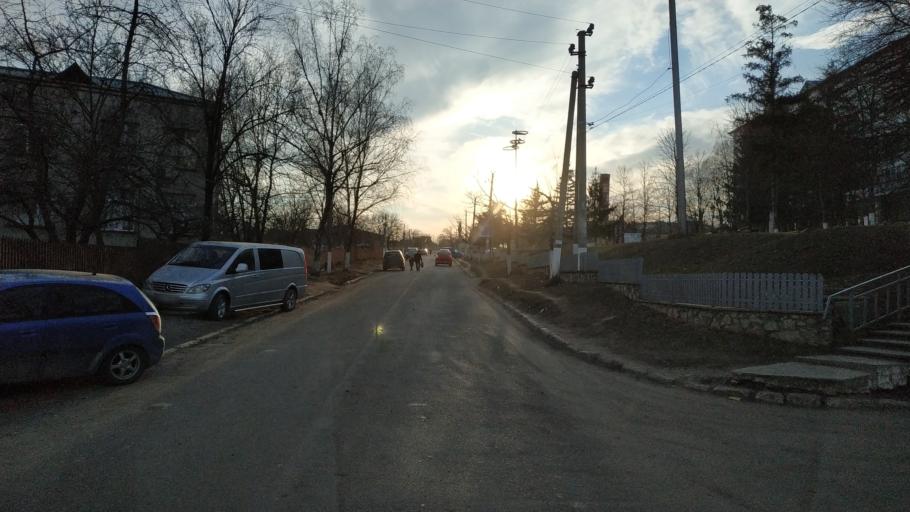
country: MD
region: Nisporeni
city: Nisporeni
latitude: 47.0881
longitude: 28.1766
